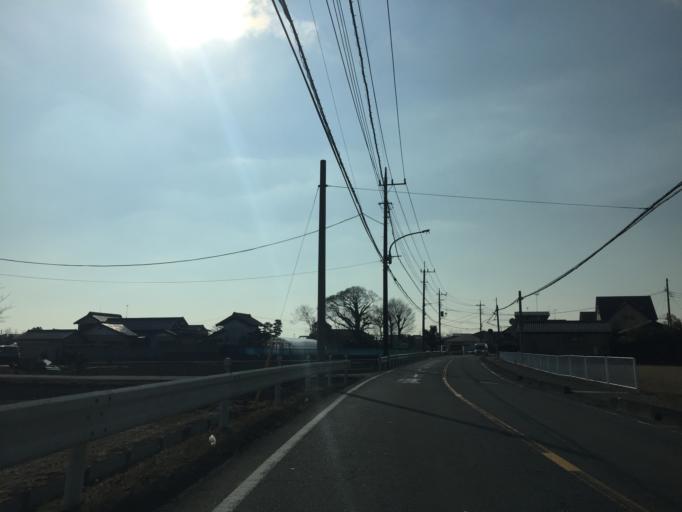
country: JP
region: Saitama
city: Kamifukuoka
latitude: 35.8788
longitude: 139.5526
